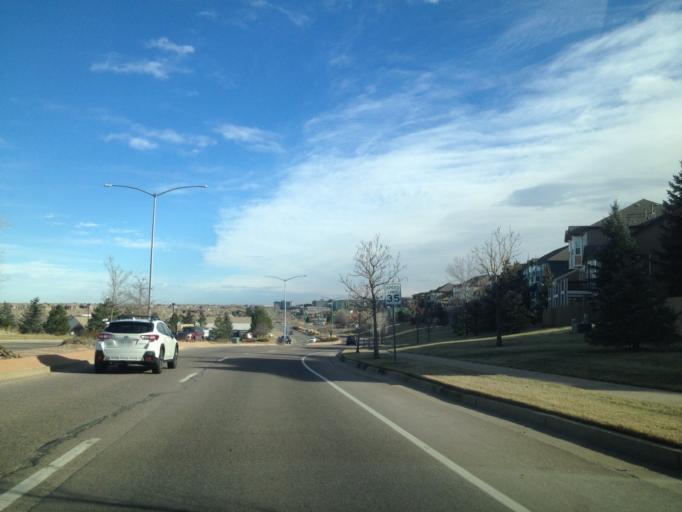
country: US
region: Colorado
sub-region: Boulder County
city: Superior
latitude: 39.9291
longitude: -105.1525
